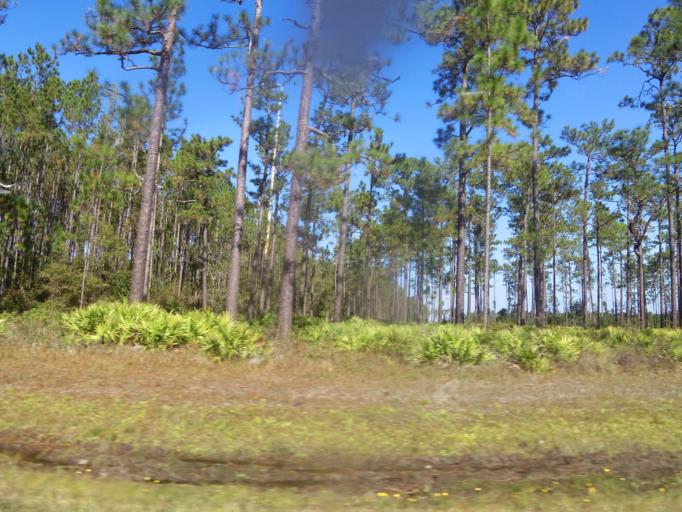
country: US
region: Georgia
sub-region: Charlton County
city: Folkston
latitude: 30.7397
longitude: -82.1016
